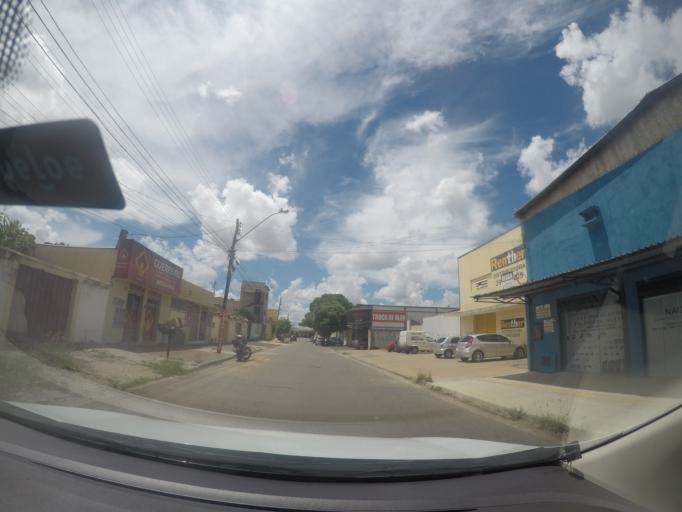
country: BR
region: Goias
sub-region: Goiania
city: Goiania
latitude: -16.6778
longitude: -49.3080
